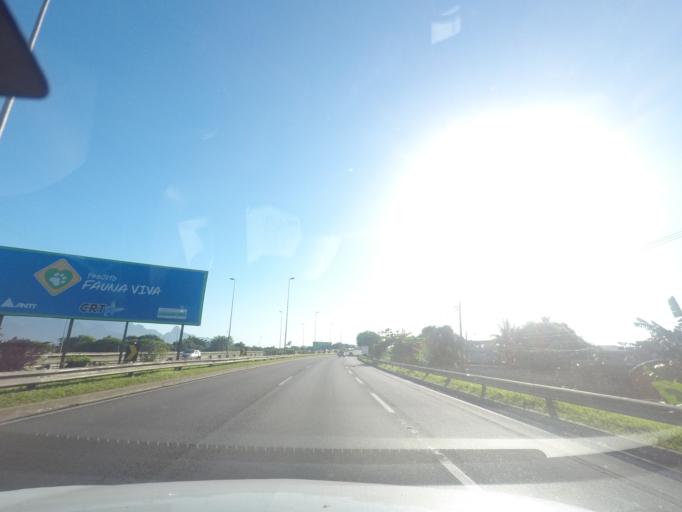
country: BR
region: Rio de Janeiro
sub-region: Petropolis
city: Petropolis
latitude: -22.6478
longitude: -43.2273
